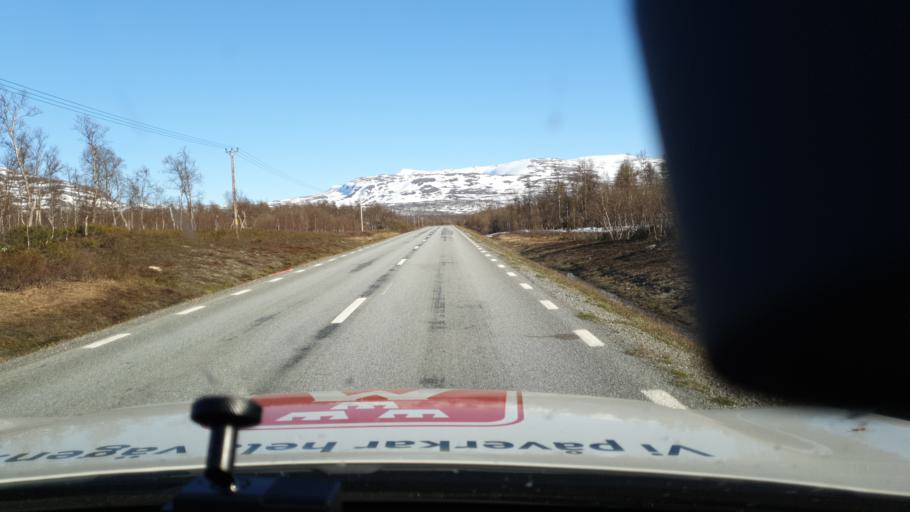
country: NO
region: Nordland
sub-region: Rana
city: Mo i Rana
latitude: 66.0330
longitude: 15.0716
